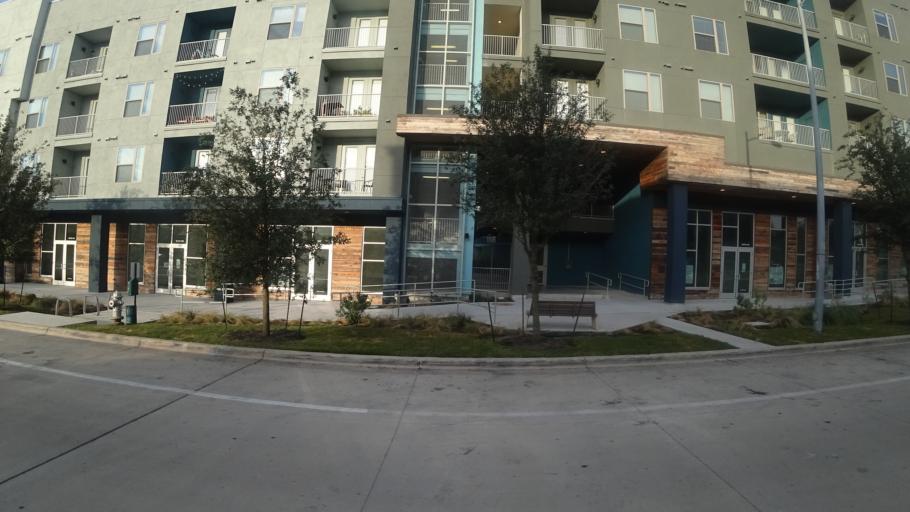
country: US
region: Texas
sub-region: Travis County
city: Austin
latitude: 30.2810
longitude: -97.7094
